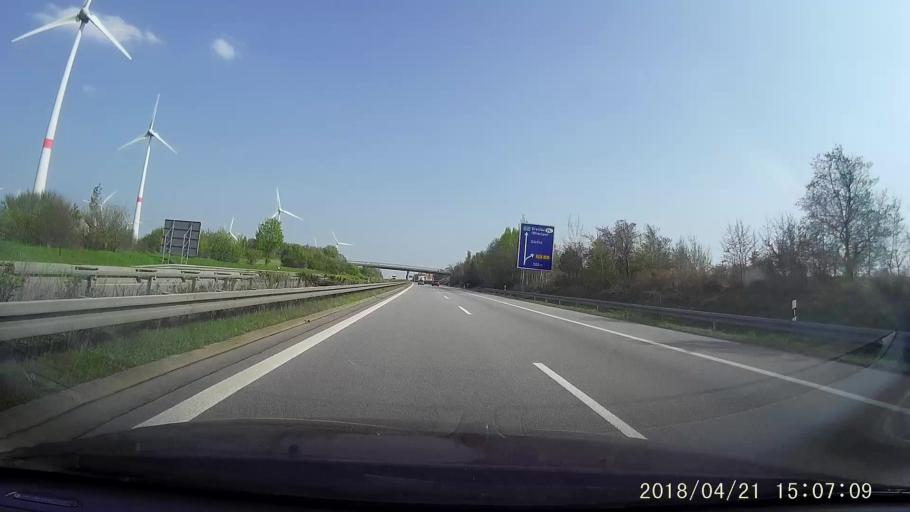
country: DE
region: Saxony
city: Goerlitz
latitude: 51.2028
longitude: 14.9537
